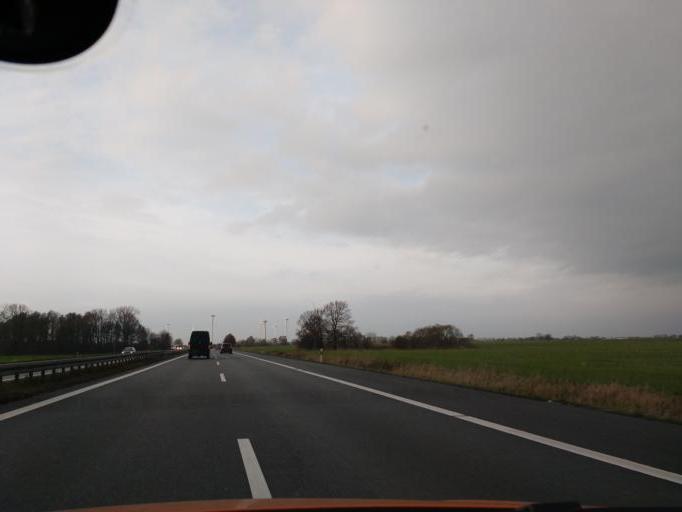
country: DE
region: Brandenburg
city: Dabergotz
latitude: 52.8907
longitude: 12.7515
